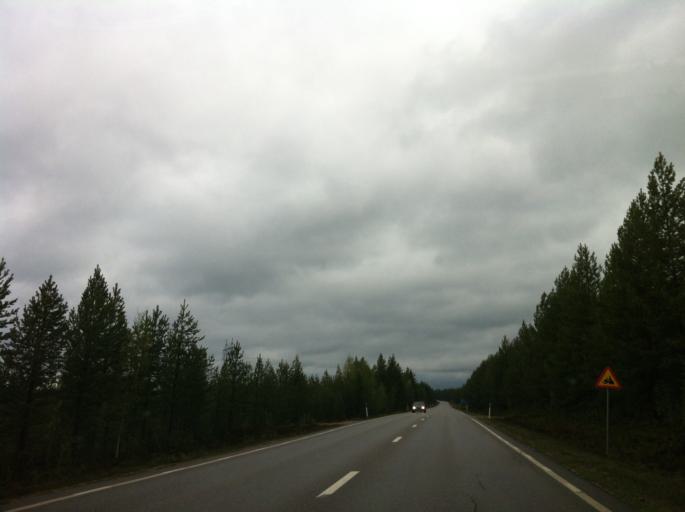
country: SE
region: Jaemtland
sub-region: Harjedalens Kommun
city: Sveg
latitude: 62.0531
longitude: 14.3075
